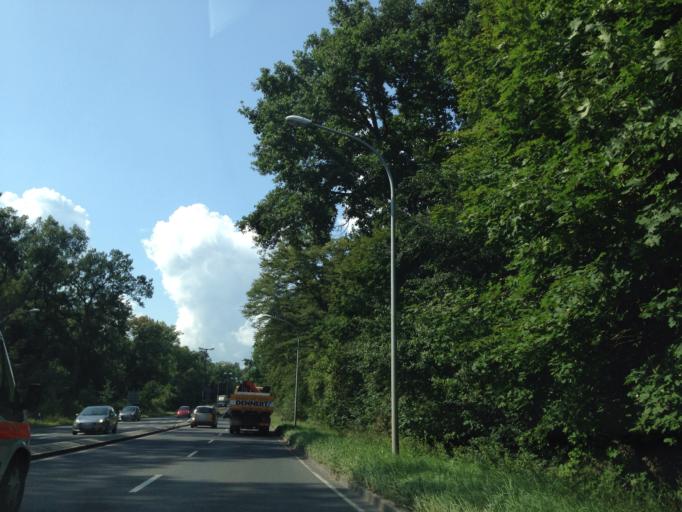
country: DE
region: Bavaria
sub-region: Upper Franconia
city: Bamberg
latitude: 49.8831
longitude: 10.9021
